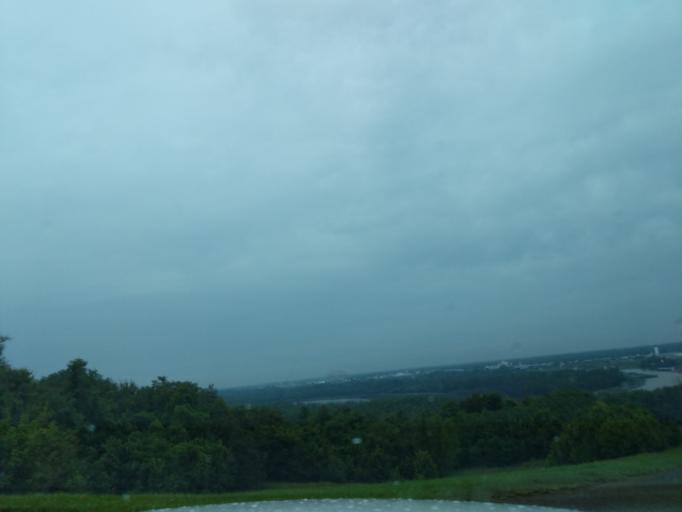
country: US
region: Mississippi
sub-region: Warren County
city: Vicksburg
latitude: 32.3687
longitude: -90.8704
